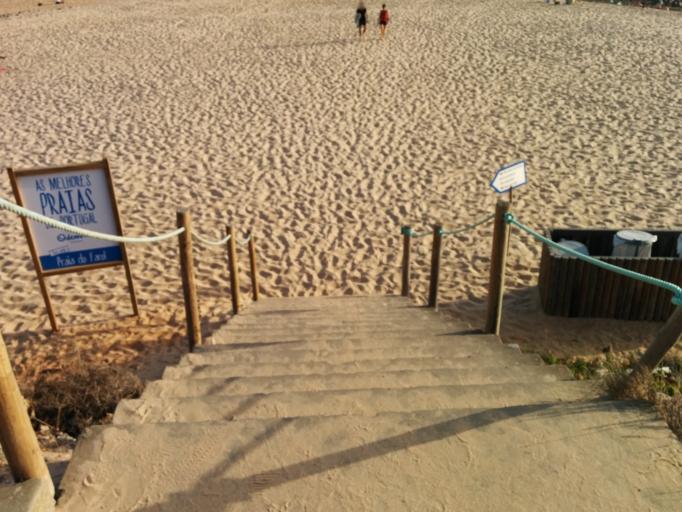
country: PT
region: Beja
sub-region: Odemira
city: Vila Nova de Milfontes
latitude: 37.7189
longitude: -8.7903
